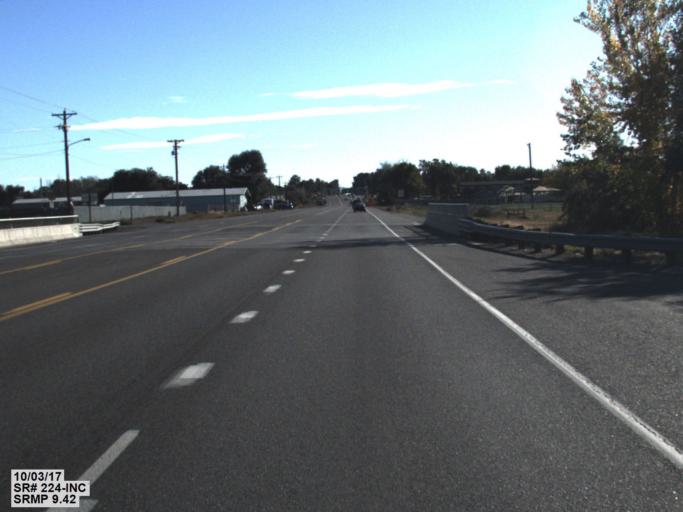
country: US
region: Washington
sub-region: Benton County
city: Richland
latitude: 46.2932
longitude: -119.3151
